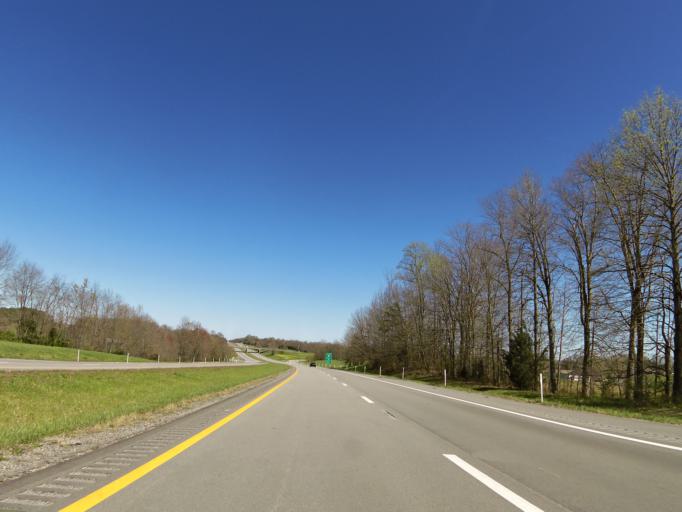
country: US
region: Kentucky
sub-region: Pulaski County
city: Somerset
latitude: 37.0915
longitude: -84.8089
